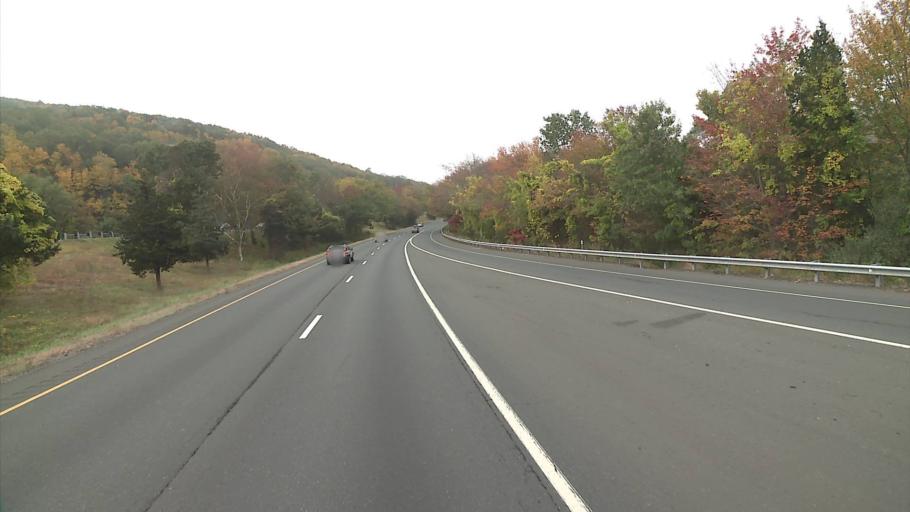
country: US
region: Connecticut
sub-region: New Haven County
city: Heritage Village
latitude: 41.4564
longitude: -73.2365
